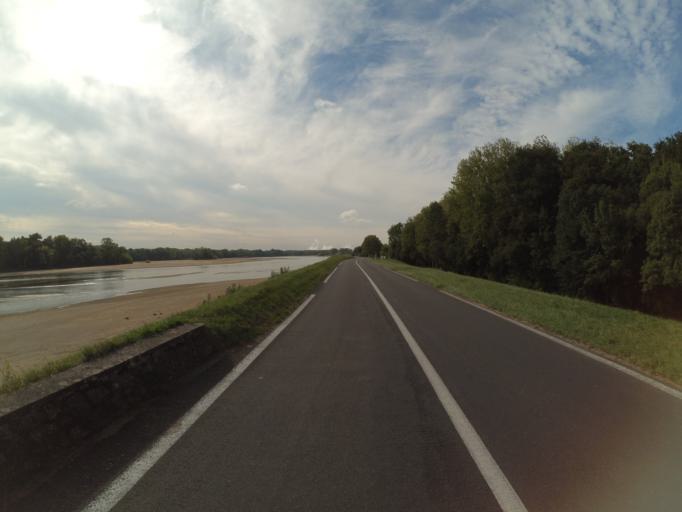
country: FR
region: Centre
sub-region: Departement d'Indre-et-Loire
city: La Chapelle-sur-Loire
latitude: 47.2443
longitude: 0.2092
